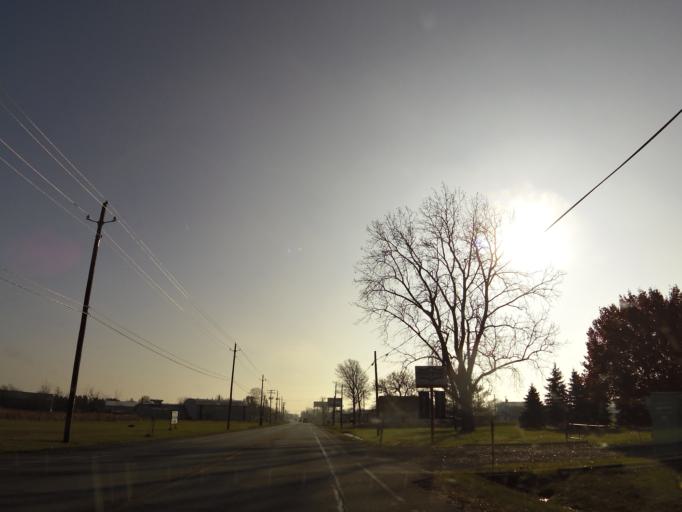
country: US
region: Indiana
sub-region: Marion County
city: Clermont
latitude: 39.8202
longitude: -86.3346
